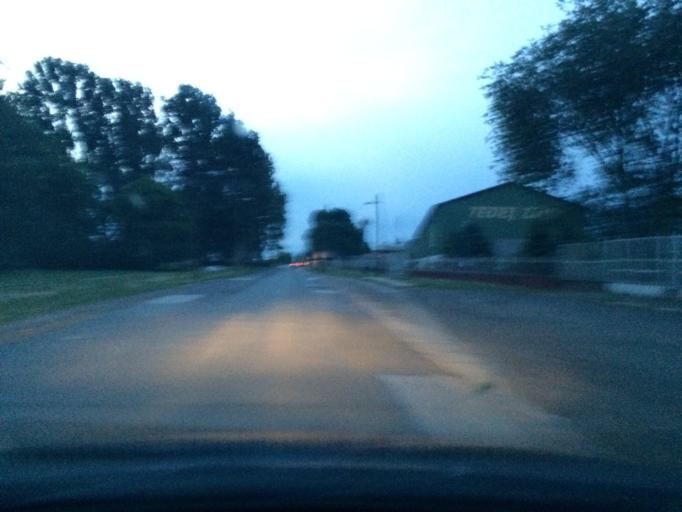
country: HU
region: Hajdu-Bihar
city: Hajdunanas
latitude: 47.9036
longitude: 21.4054
